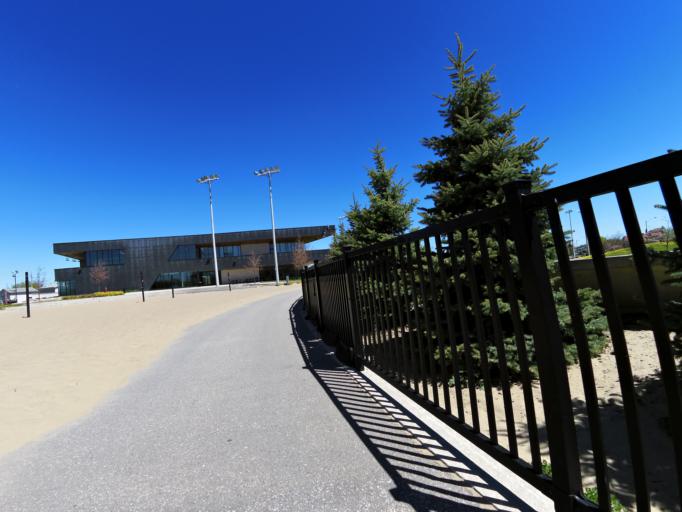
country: CA
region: Ontario
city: Brampton
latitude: 43.7268
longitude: -79.7237
